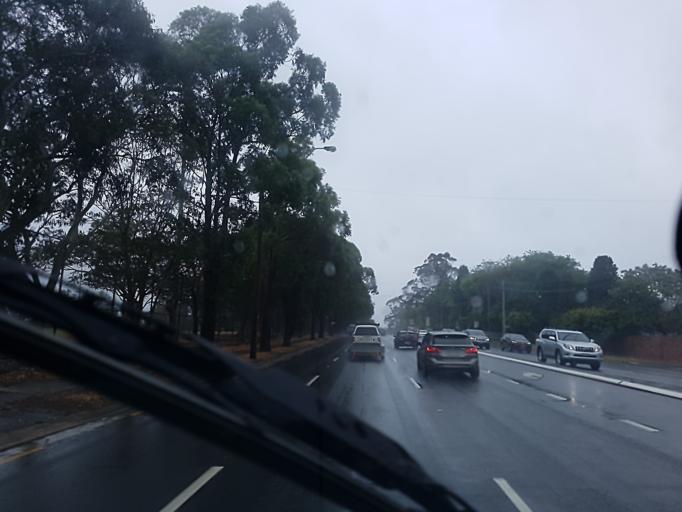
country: AU
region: New South Wales
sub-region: City of Sydney
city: North Turramurra
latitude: -33.7170
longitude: 151.1731
